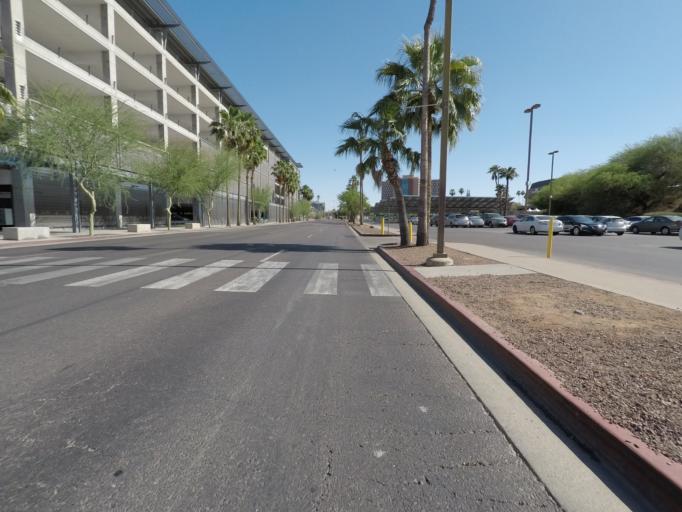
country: US
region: Arizona
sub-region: Maricopa County
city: Tempe Junction
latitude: 33.4262
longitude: -111.9293
